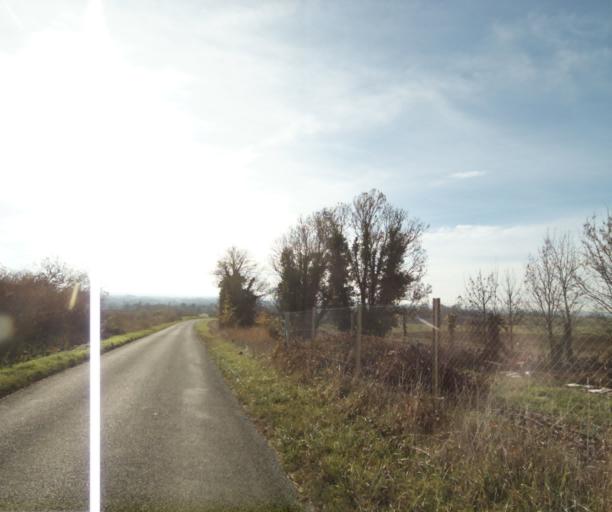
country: FR
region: Poitou-Charentes
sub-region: Departement de la Charente-Maritime
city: Chaniers
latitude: 45.7265
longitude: -0.5519
